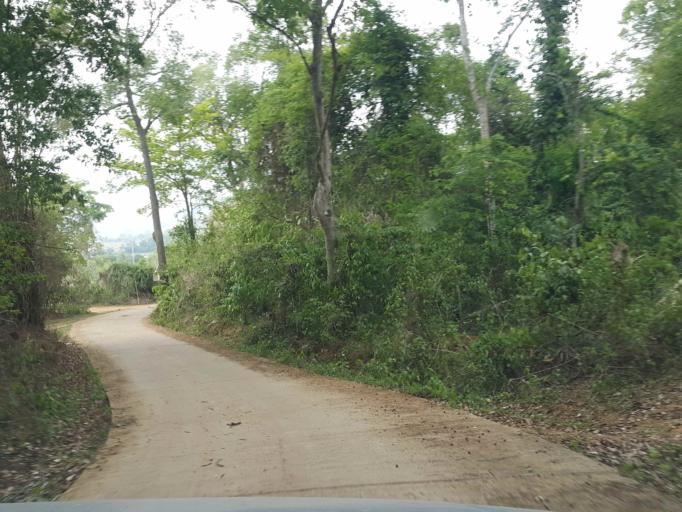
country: TH
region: Chiang Mai
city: Wiang Haeng
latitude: 19.3726
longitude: 98.7196
